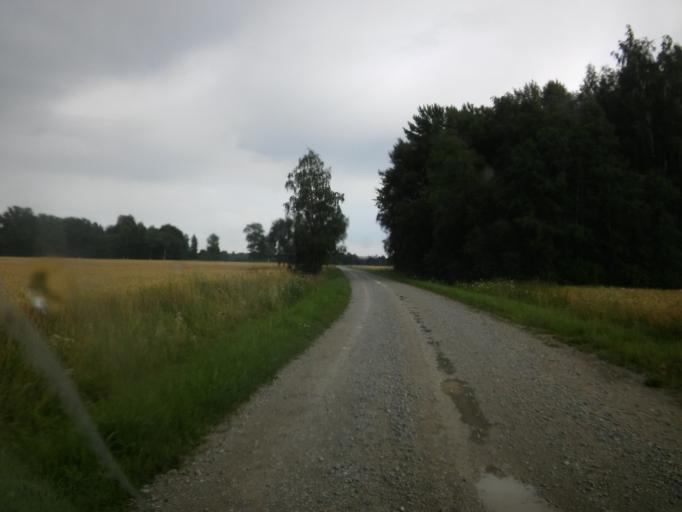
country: EE
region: Raplamaa
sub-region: Maerjamaa vald
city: Marjamaa
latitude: 58.7810
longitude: 24.5424
